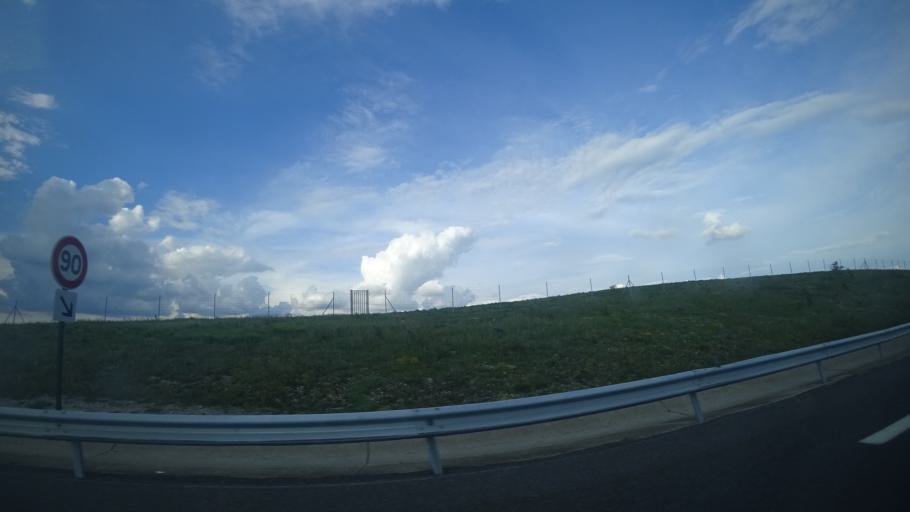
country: FR
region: Midi-Pyrenees
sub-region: Departement de l'Aveyron
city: Creissels
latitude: 44.0305
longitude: 3.0682
